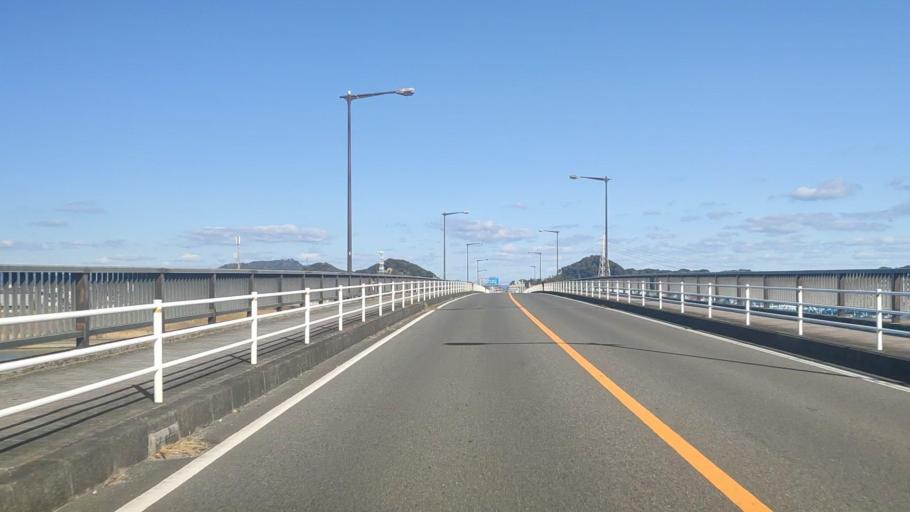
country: JP
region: Oita
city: Saiki
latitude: 32.9478
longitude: 131.9022
